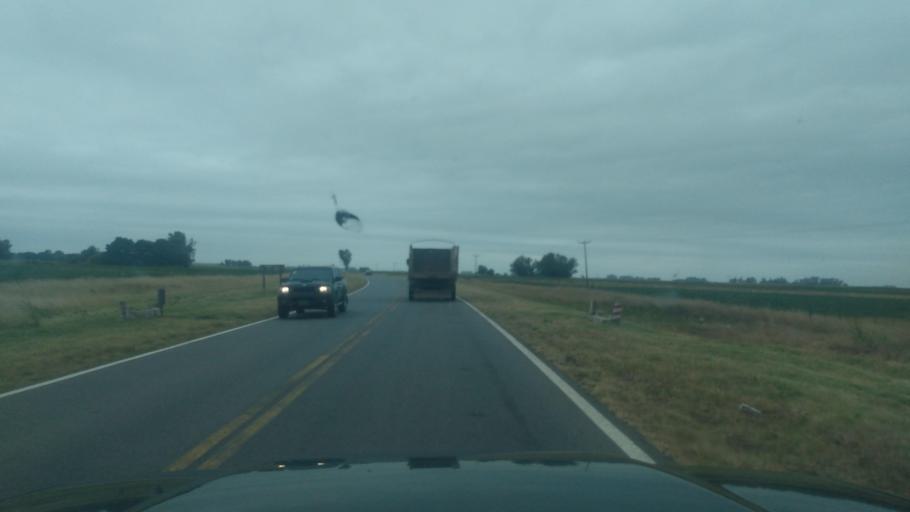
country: AR
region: Buenos Aires
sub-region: Partido de Nueve de Julio
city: Nueve de Julio
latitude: -35.3961
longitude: -60.7443
